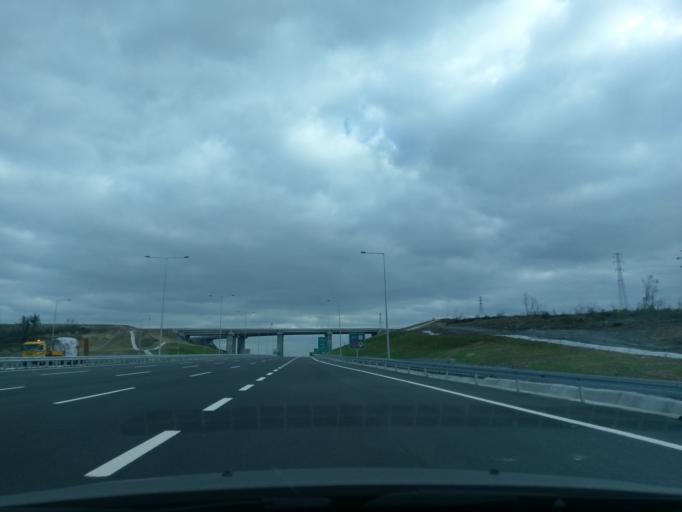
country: TR
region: Istanbul
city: Durusu
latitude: 41.2451
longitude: 28.6895
